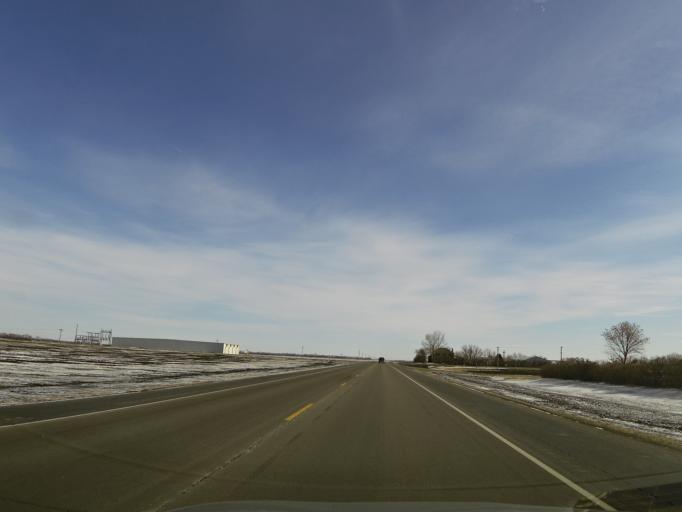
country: US
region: North Dakota
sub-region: Walsh County
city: Grafton
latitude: 48.4126
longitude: -97.3466
